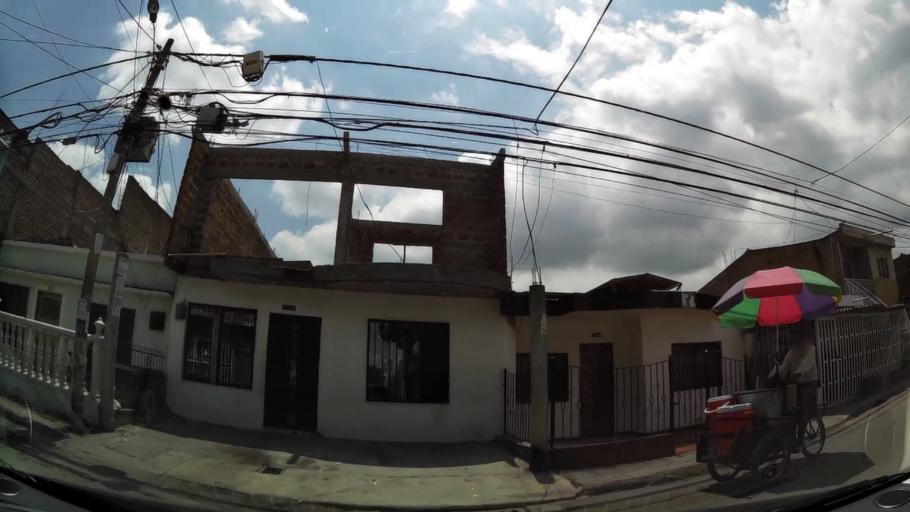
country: CO
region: Valle del Cauca
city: Cali
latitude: 3.4649
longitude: -76.4818
